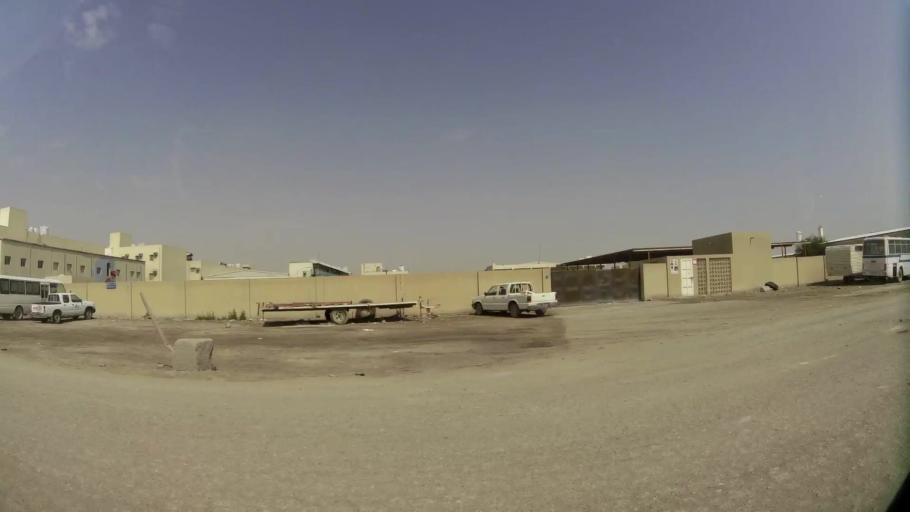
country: QA
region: Al Wakrah
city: Al Wukayr
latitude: 25.1700
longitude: 51.4514
